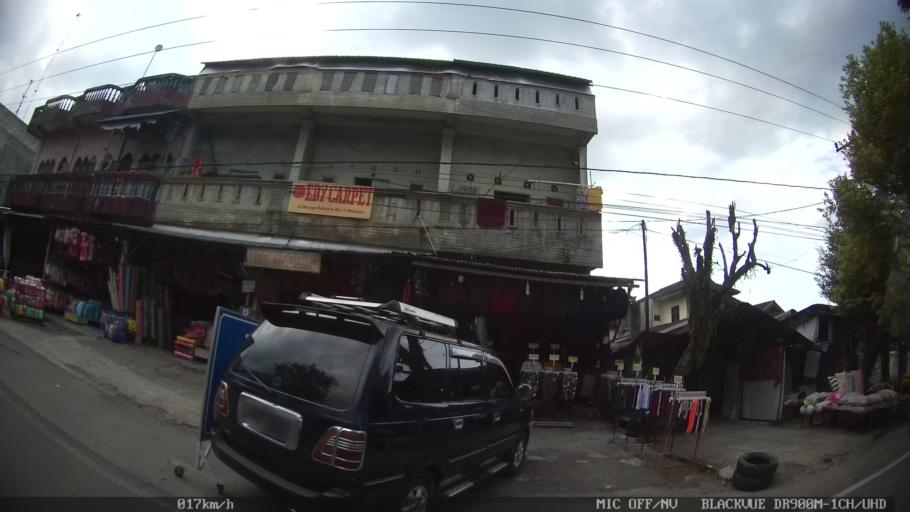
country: ID
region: North Sumatra
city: Sunggal
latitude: 3.5419
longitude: 98.6046
